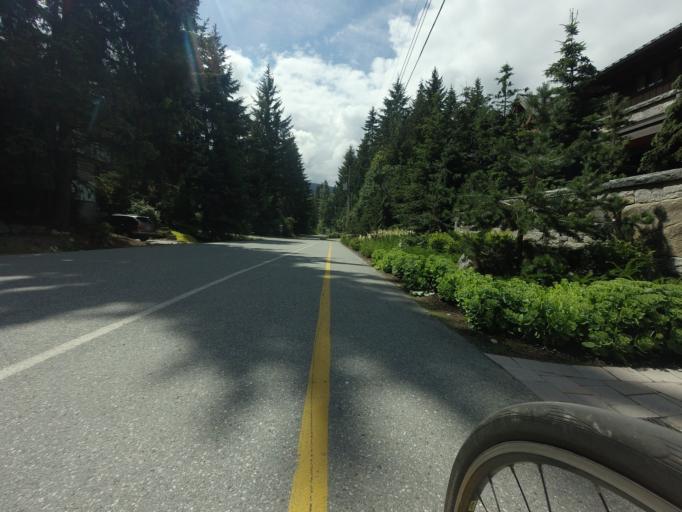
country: CA
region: British Columbia
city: Whistler
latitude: 50.1086
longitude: -122.9787
